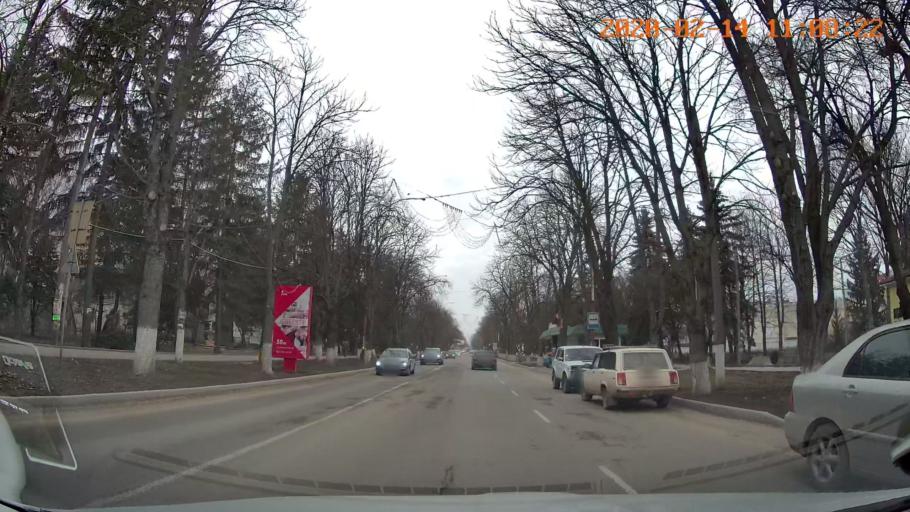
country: MD
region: Raionul Edinet
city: Edinet
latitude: 48.1716
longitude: 27.3028
